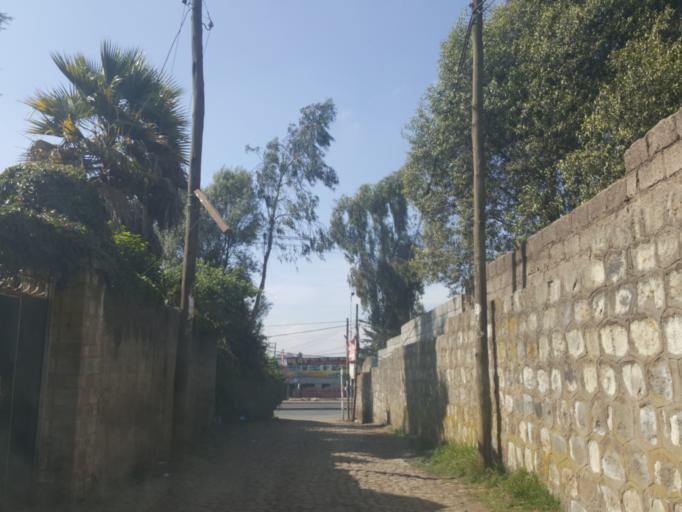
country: ET
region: Adis Abeba
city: Addis Ababa
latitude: 9.0512
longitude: 38.7239
